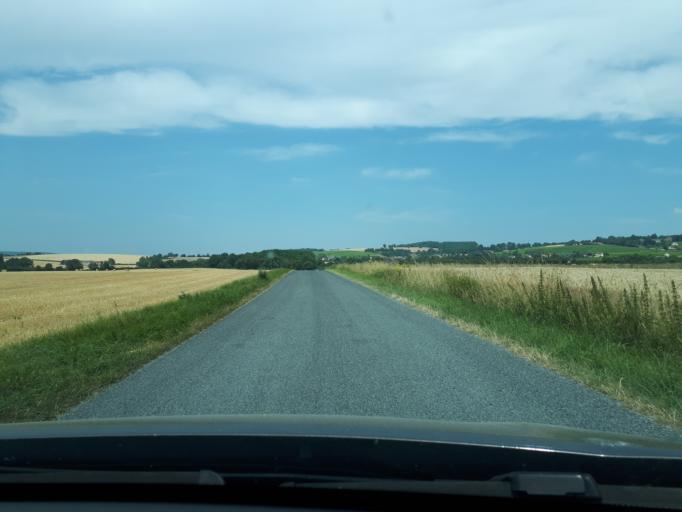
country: FR
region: Centre
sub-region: Departement du Cher
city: Sancerre
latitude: 47.2930
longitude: 2.7541
